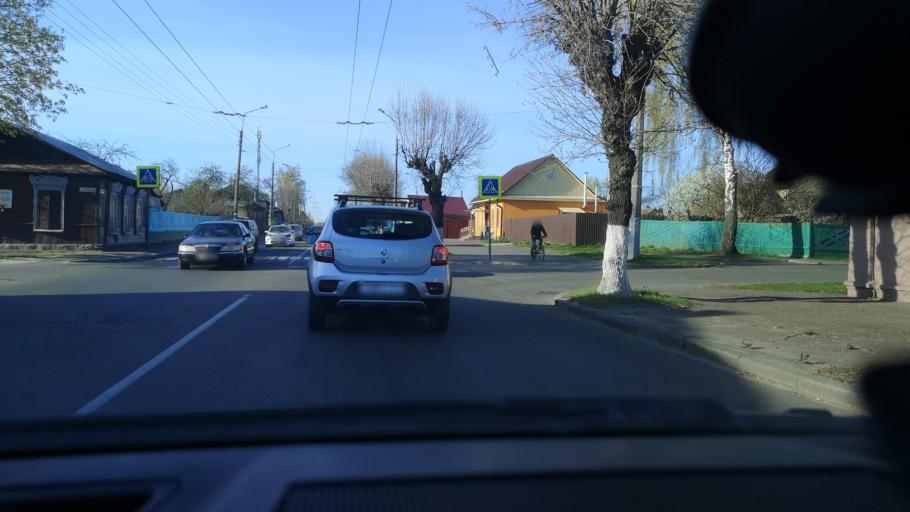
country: BY
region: Gomel
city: Gomel
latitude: 52.4357
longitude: 30.9767
